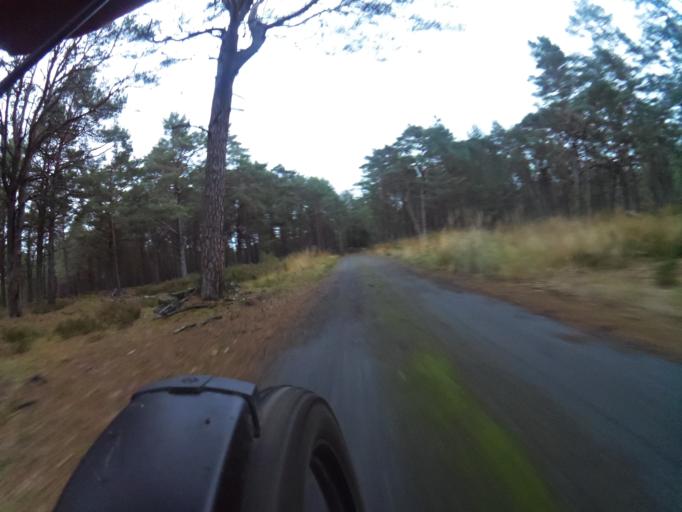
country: PL
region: Pomeranian Voivodeship
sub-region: Powiat wejherowski
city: Choczewo
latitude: 54.7958
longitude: 17.7765
